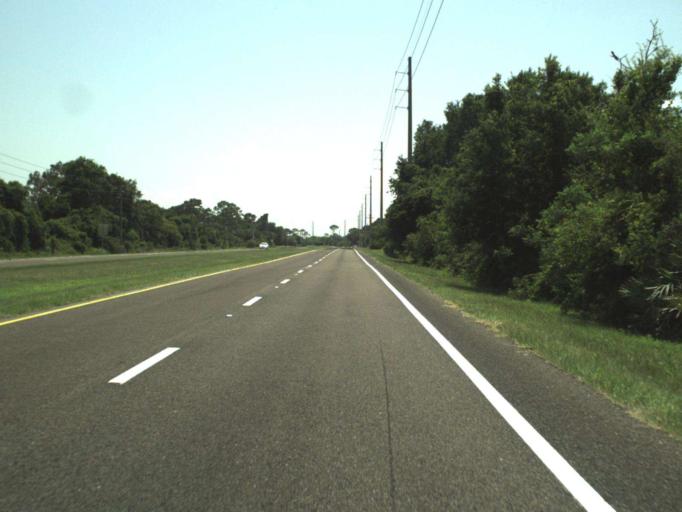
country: US
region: Florida
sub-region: Volusia County
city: Oak Hill
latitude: 28.7943
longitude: -80.8820
